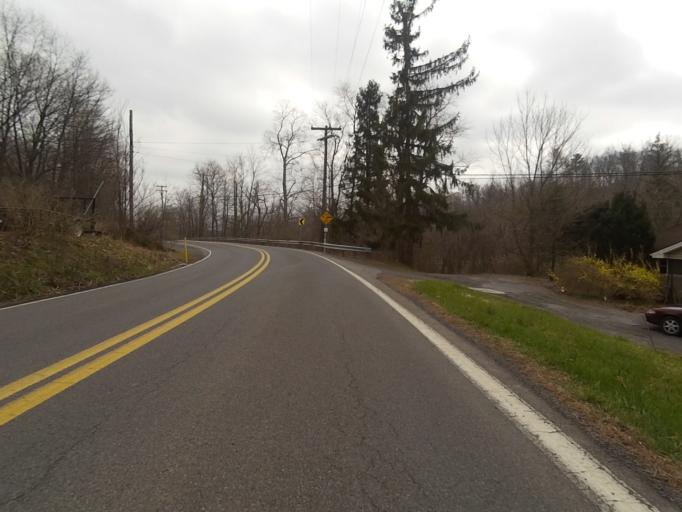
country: US
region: Pennsylvania
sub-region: Centre County
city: Lemont
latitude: 40.8053
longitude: -77.8183
